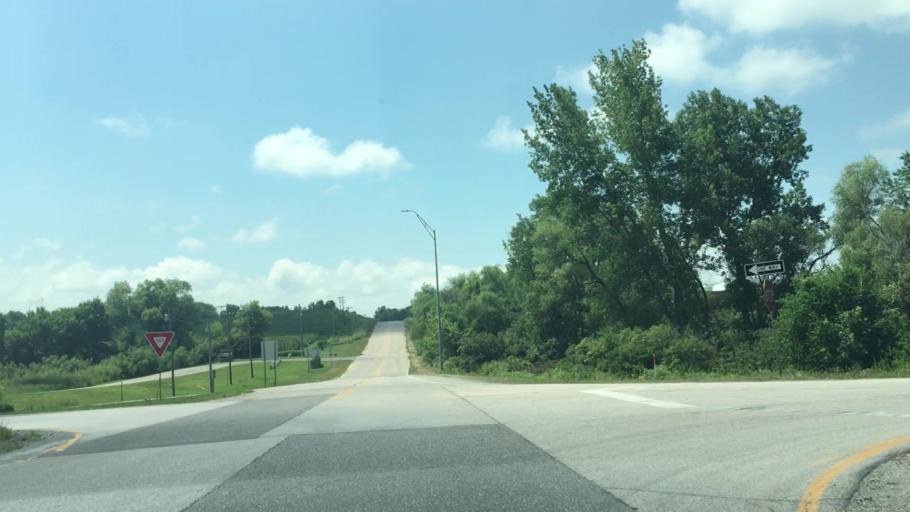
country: US
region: Iowa
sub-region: Johnson County
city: Tiffin
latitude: 41.6925
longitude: -91.6665
